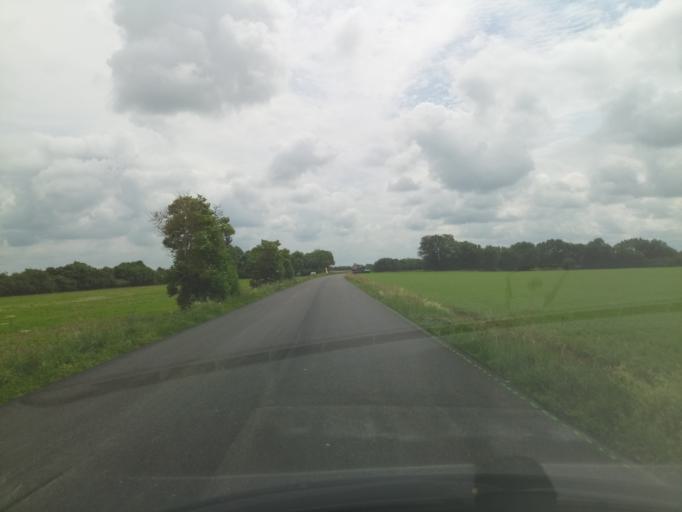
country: FR
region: Poitou-Charentes
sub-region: Departement de la Charente-Maritime
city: Saint-Jean-de-Liversay
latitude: 46.2747
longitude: -0.9082
